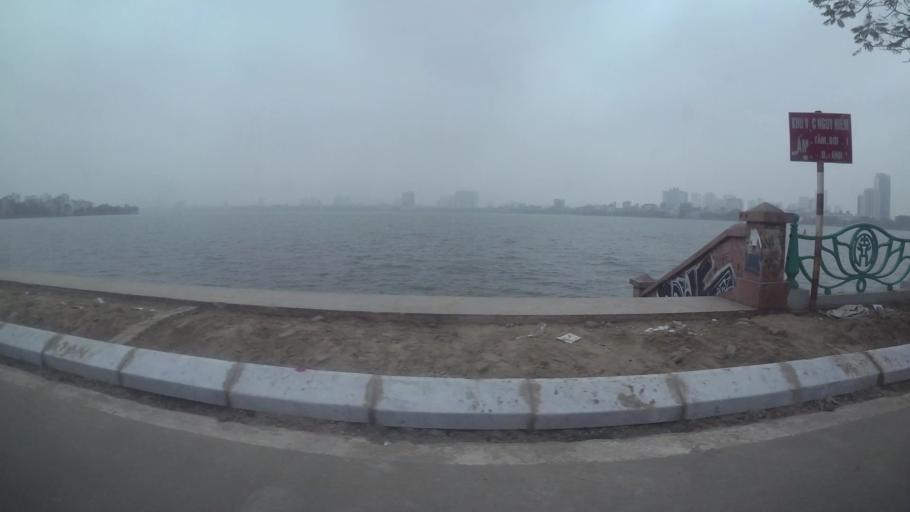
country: VN
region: Ha Noi
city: Tay Ho
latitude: 21.0665
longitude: 105.8191
